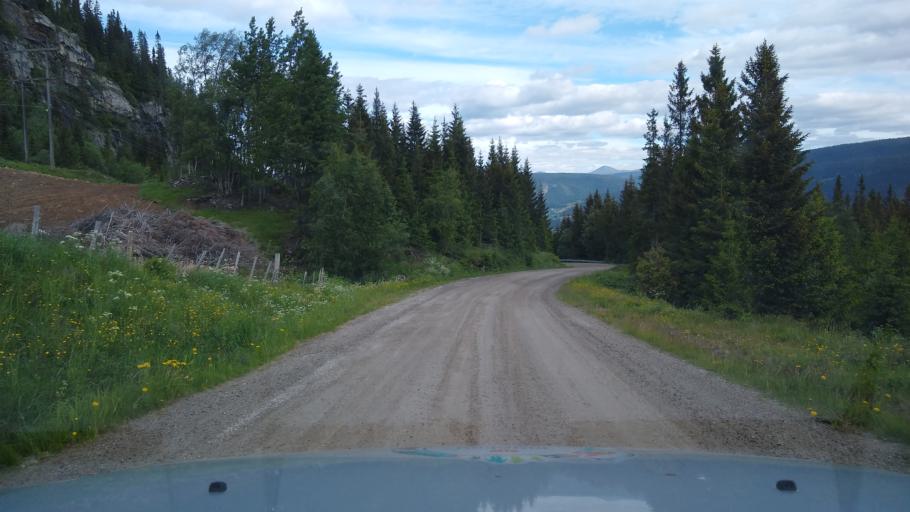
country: NO
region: Oppland
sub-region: Ringebu
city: Ringebu
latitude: 61.4949
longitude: 10.1452
